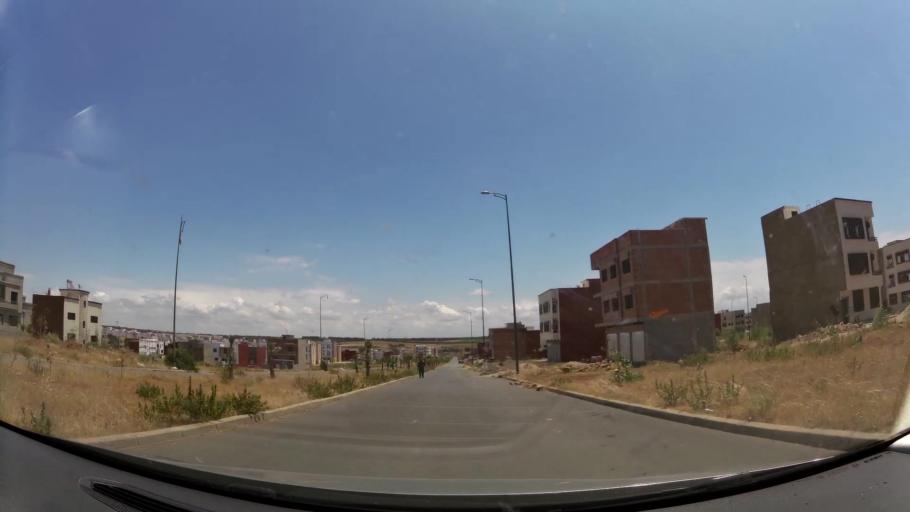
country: MA
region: Gharb-Chrarda-Beni Hssen
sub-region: Kenitra Province
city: Kenitra
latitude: 34.2480
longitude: -6.6594
